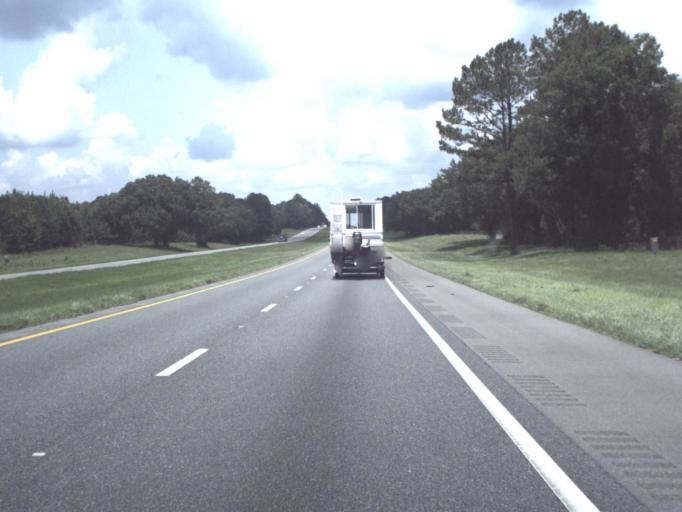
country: US
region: Florida
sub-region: Columbia County
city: Five Points
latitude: 30.2526
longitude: -82.7117
